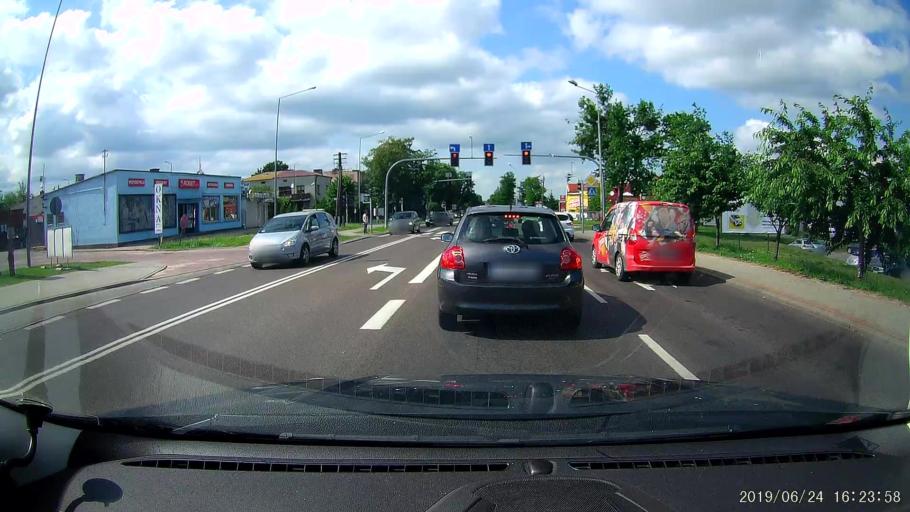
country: PL
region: Lublin Voivodeship
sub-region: Powiat tomaszowski
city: Tomaszow Lubelski
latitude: 50.4358
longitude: 23.4201
